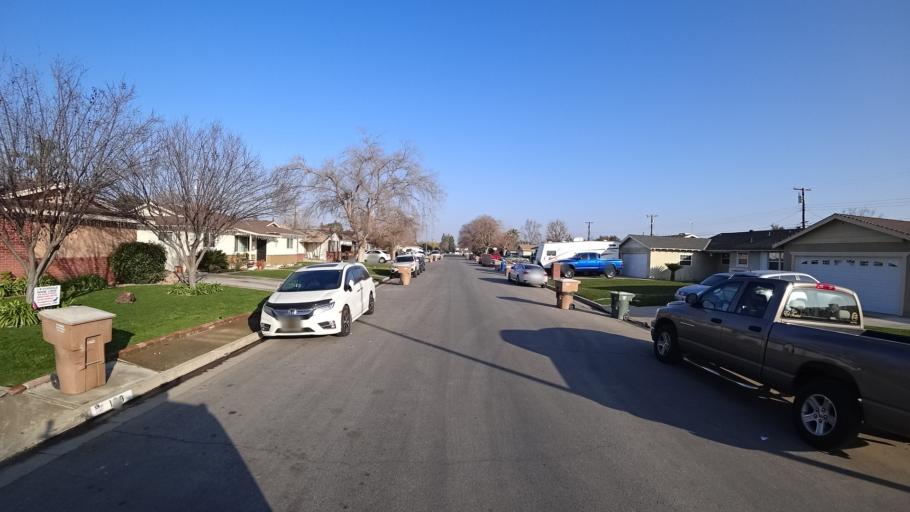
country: US
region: California
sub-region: Kern County
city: Bakersfield
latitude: 35.3559
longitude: -119.0517
